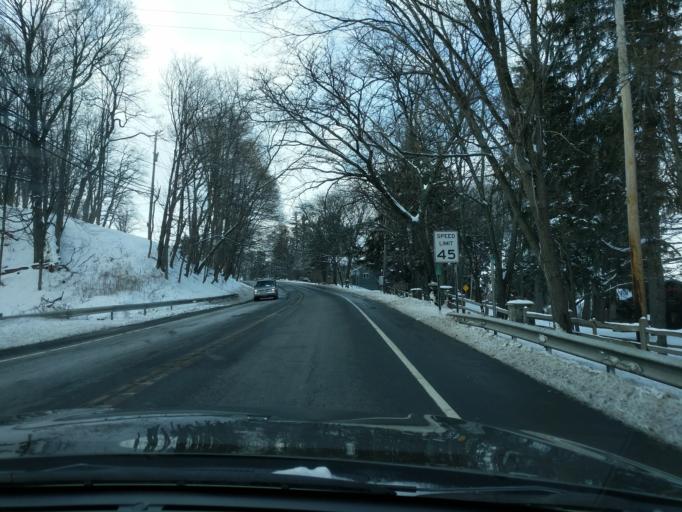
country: US
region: New York
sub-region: Tompkins County
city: Northwest Ithaca
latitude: 42.4572
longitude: -76.5245
